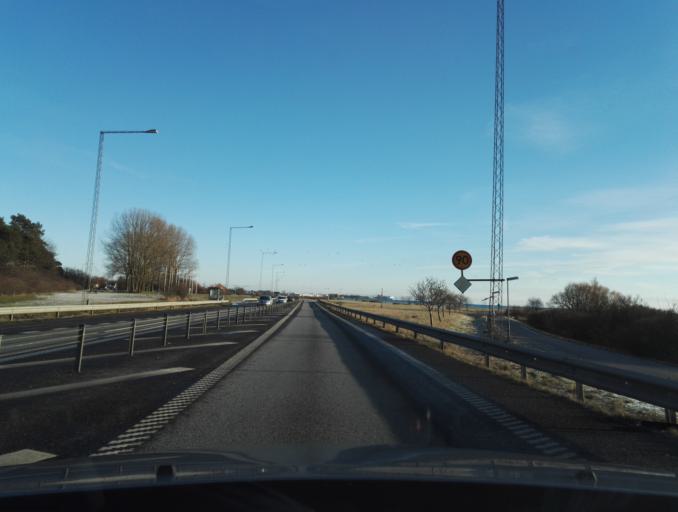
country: SE
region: Skane
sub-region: Trelleborgs Kommun
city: Skare
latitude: 55.3773
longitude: 13.0972
